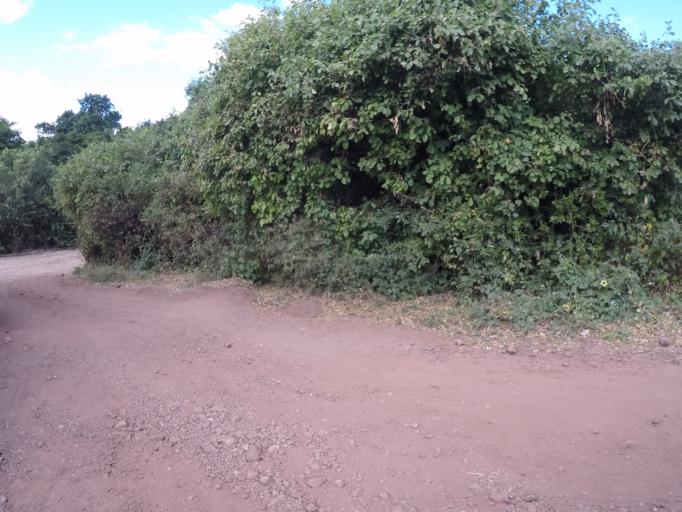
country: TZ
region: Arusha
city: Mto wa Mbu
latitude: -3.3712
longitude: 35.8397
